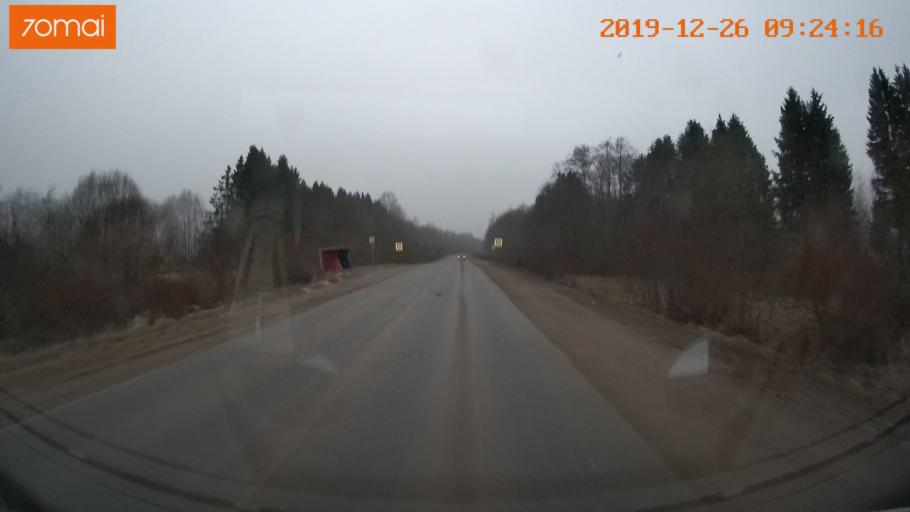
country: RU
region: Vologda
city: Gryazovets
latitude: 58.9987
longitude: 40.2004
